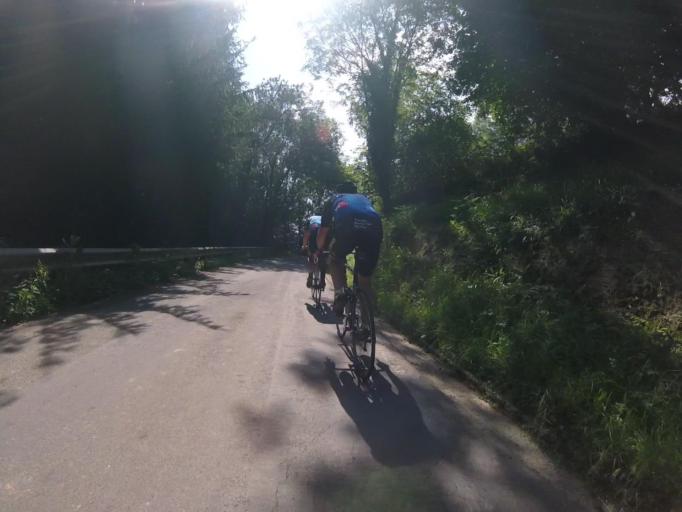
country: ES
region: Basque Country
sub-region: Provincia de Guipuzcoa
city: Orendain
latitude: 43.0773
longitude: -2.1069
